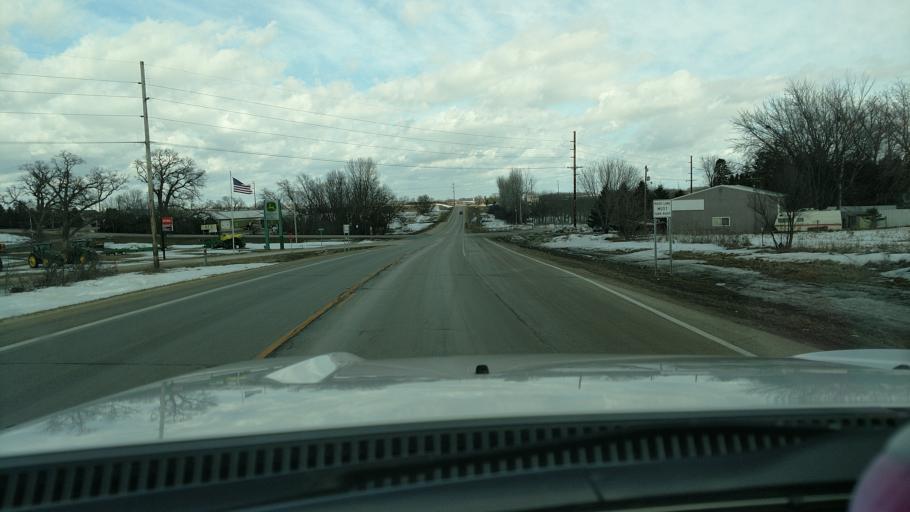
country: US
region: Minnesota
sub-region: Wabasha County
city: Plainview
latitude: 44.1786
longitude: -92.1612
